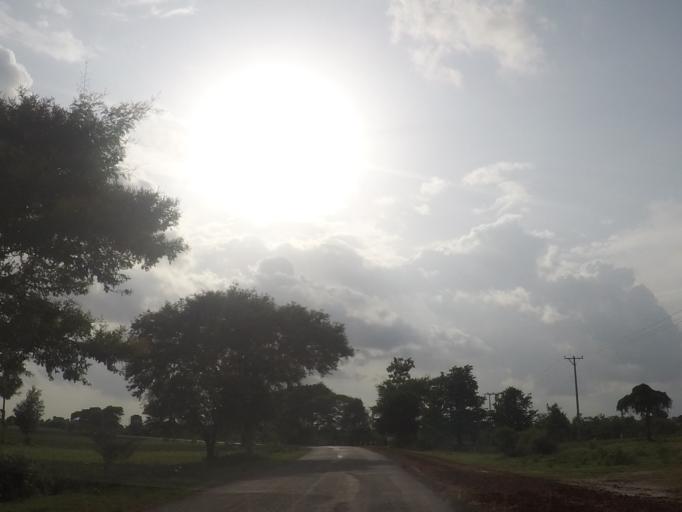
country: MM
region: Mandalay
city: Yamethin
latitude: 20.4932
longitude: 95.8133
